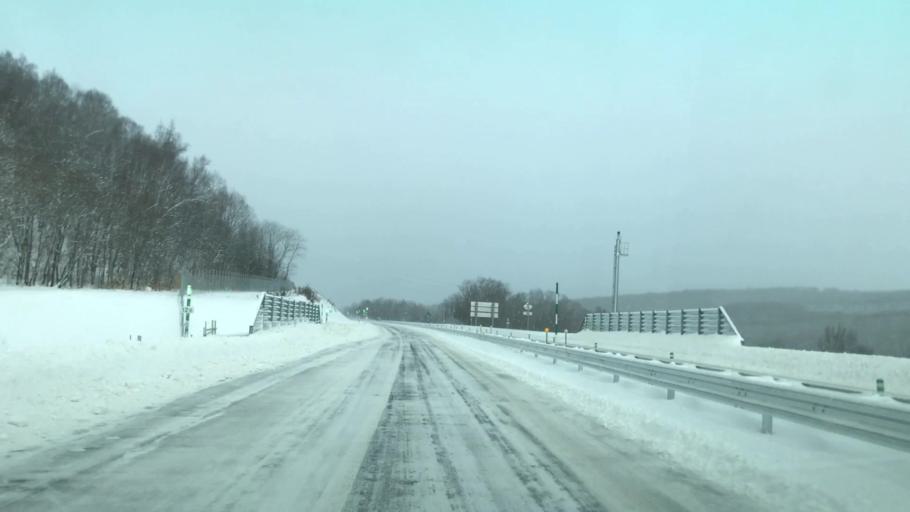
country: JP
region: Hokkaido
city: Otaru
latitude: 43.1972
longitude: 140.9496
